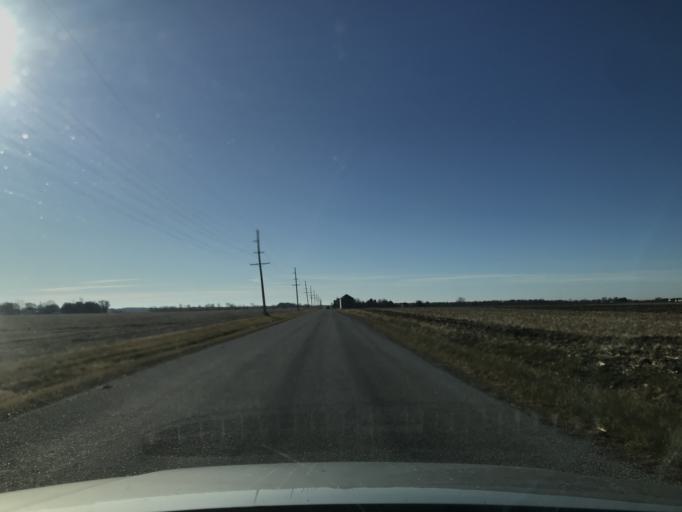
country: US
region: Illinois
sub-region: Hancock County
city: Carthage
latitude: 40.4755
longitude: -91.1781
